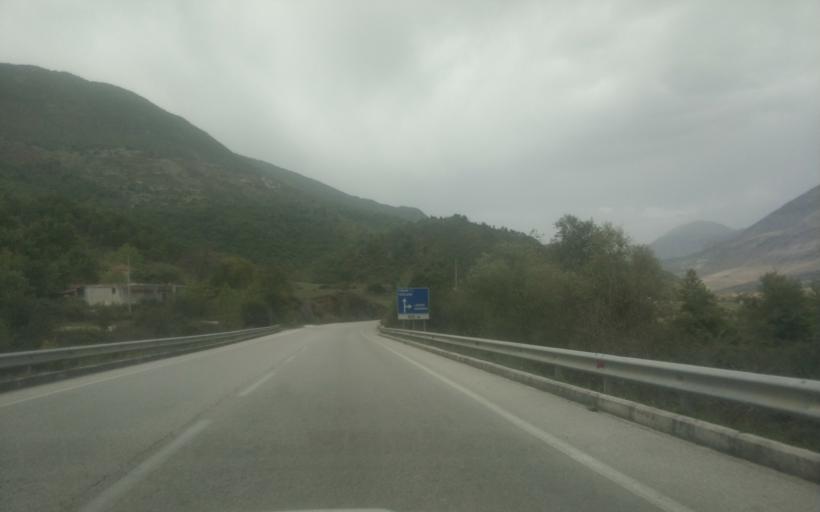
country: AL
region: Gjirokaster
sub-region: Rrethi i Gjirokastres
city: Picar
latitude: 40.2045
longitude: 20.0904
